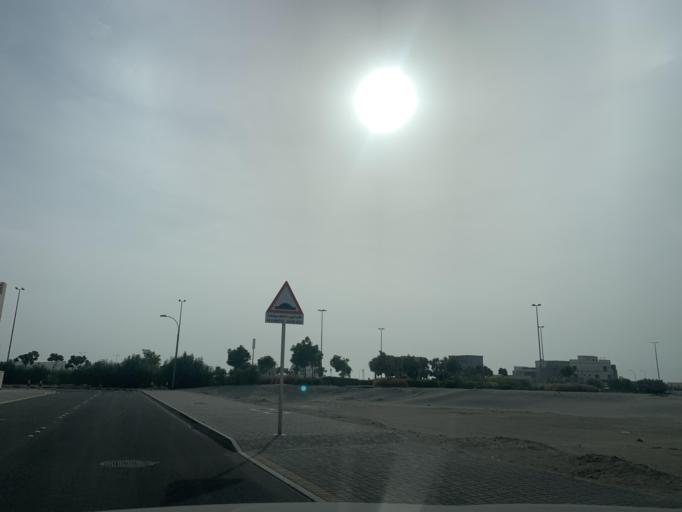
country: BH
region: Muharraq
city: Al Muharraq
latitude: 26.3188
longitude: 50.6266
